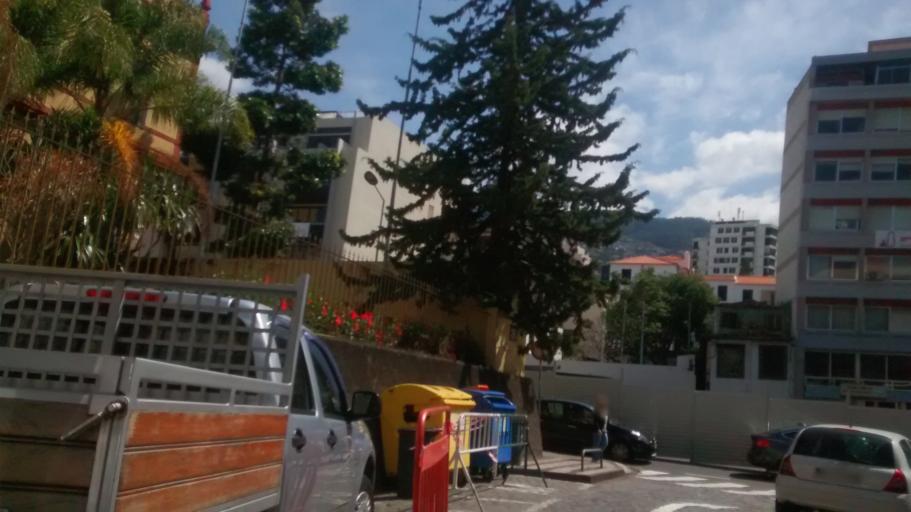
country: PT
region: Madeira
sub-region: Funchal
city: Nossa Senhora do Monte
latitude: 32.6508
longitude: -16.9087
